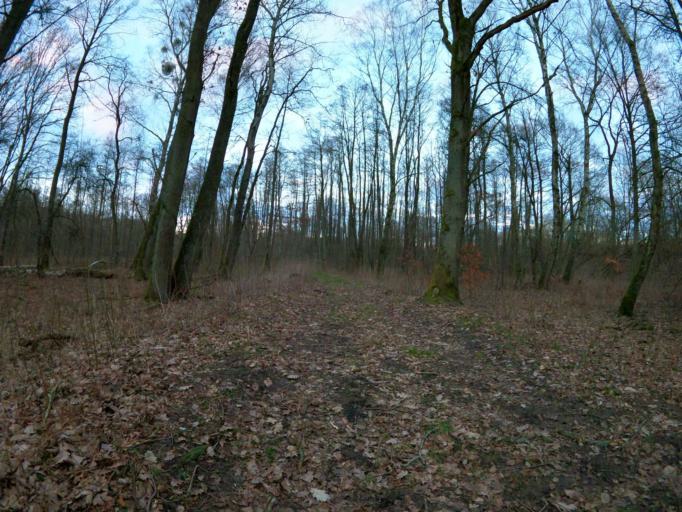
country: PL
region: West Pomeranian Voivodeship
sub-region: Powiat kamienski
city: Golczewo
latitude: 53.8303
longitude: 14.9518
